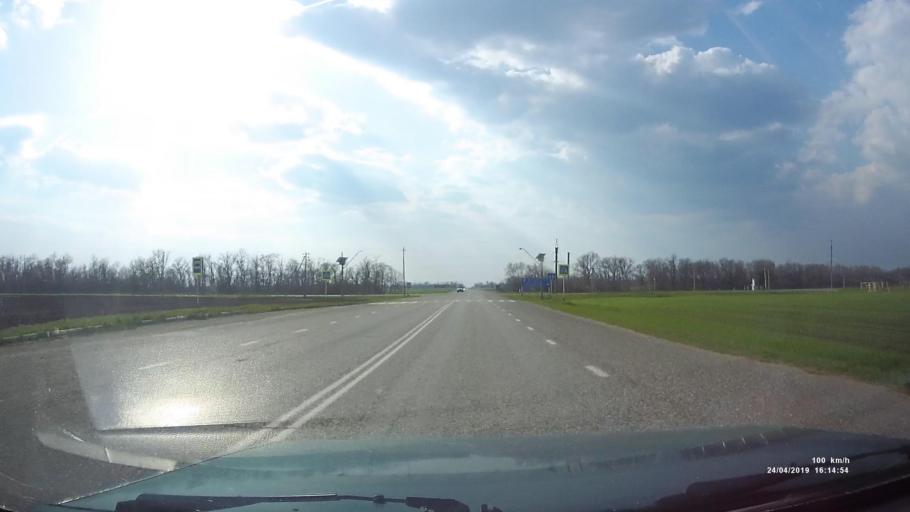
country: RU
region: Rostov
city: Sovetskoye
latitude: 46.7545
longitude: 42.1928
